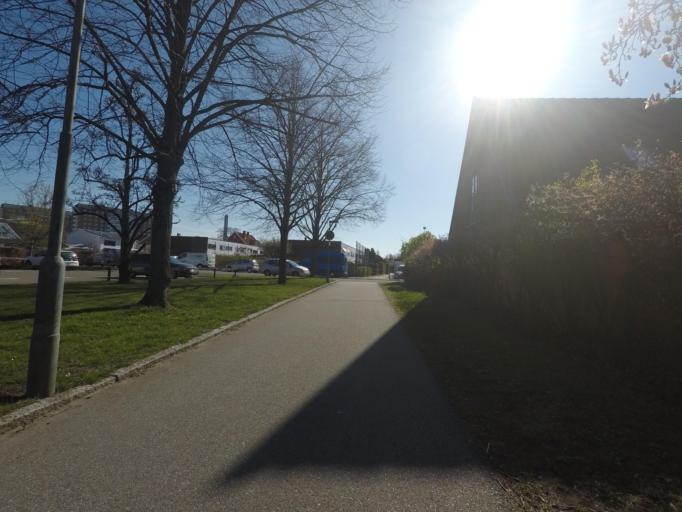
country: SE
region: Skane
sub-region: Malmo
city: Malmoe
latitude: 55.5759
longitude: 12.9974
